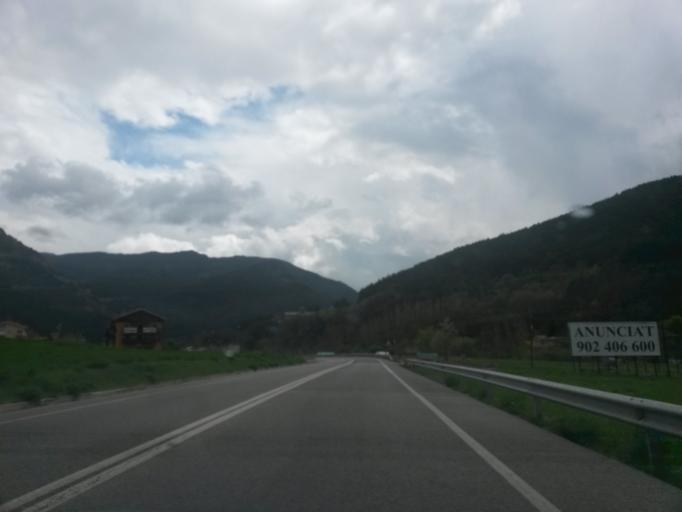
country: ES
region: Catalonia
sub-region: Provincia de Barcelona
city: Guardiola de Bergueda
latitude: 42.2409
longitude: 1.8737
